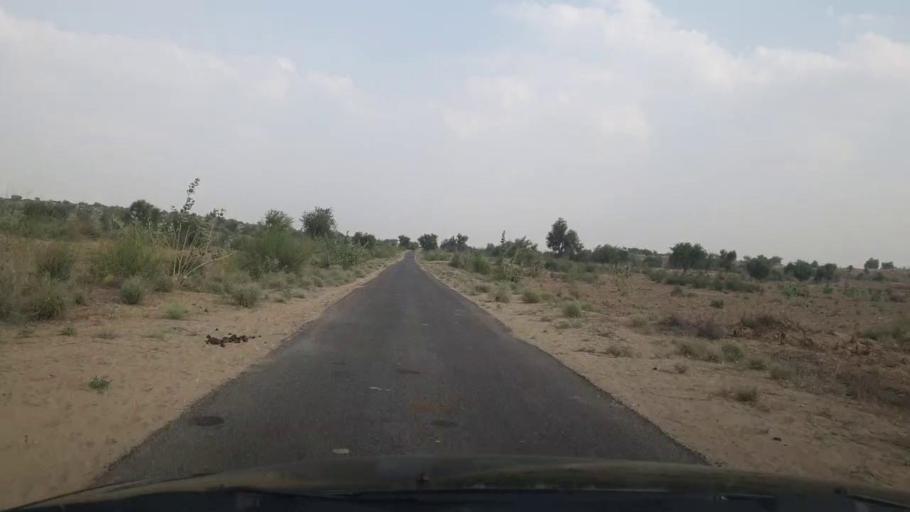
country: PK
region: Sindh
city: Islamkot
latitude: 25.0108
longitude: 70.6399
